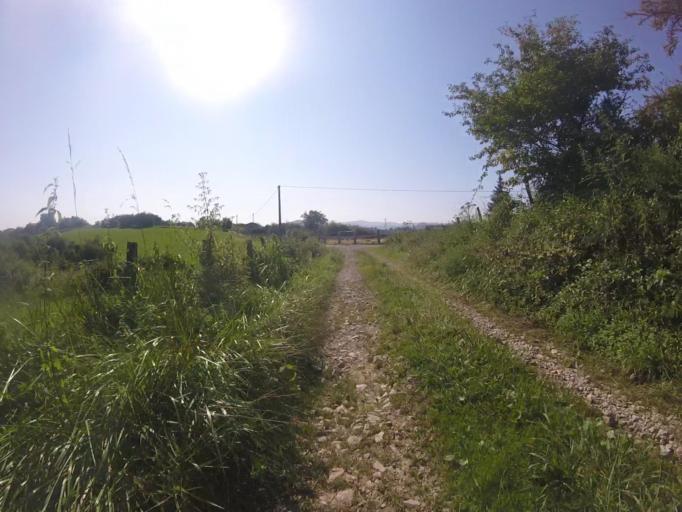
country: ES
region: Basque Country
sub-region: Provincia de Guipuzcoa
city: Astigarraga
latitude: 43.2585
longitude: -1.9385
